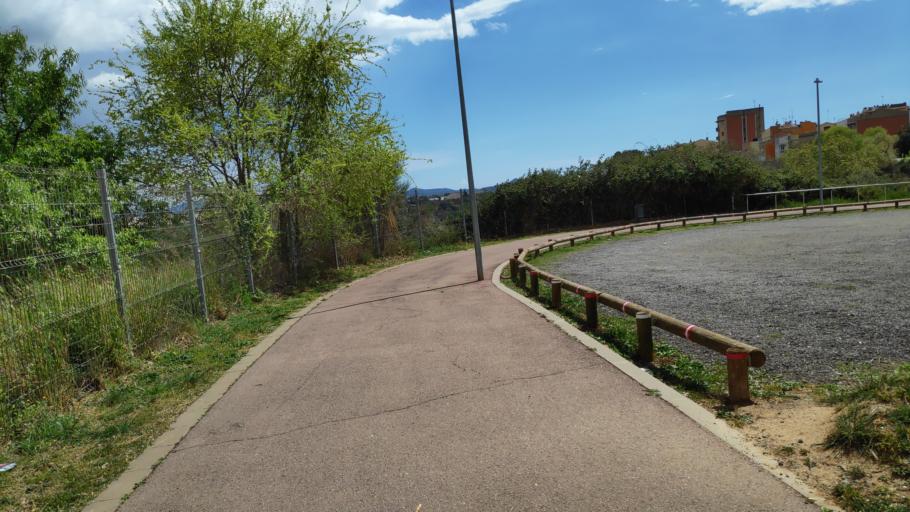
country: ES
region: Catalonia
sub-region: Provincia de Barcelona
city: Sabadell
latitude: 41.5467
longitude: 2.1201
